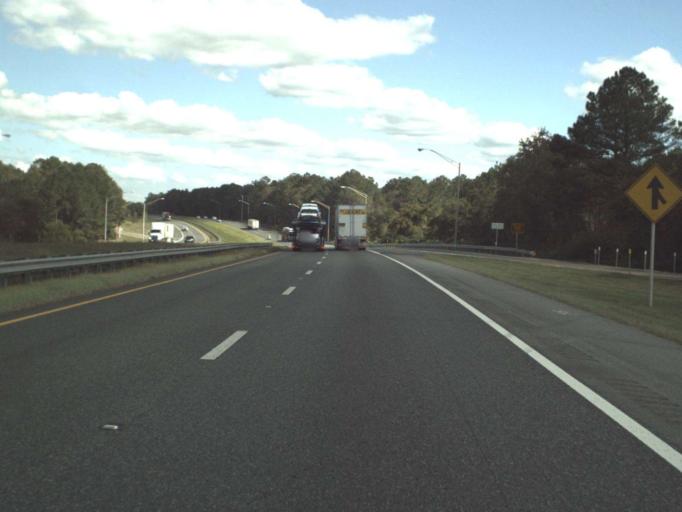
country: US
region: Florida
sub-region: Jackson County
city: Marianna
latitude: 30.7566
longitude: -85.3277
